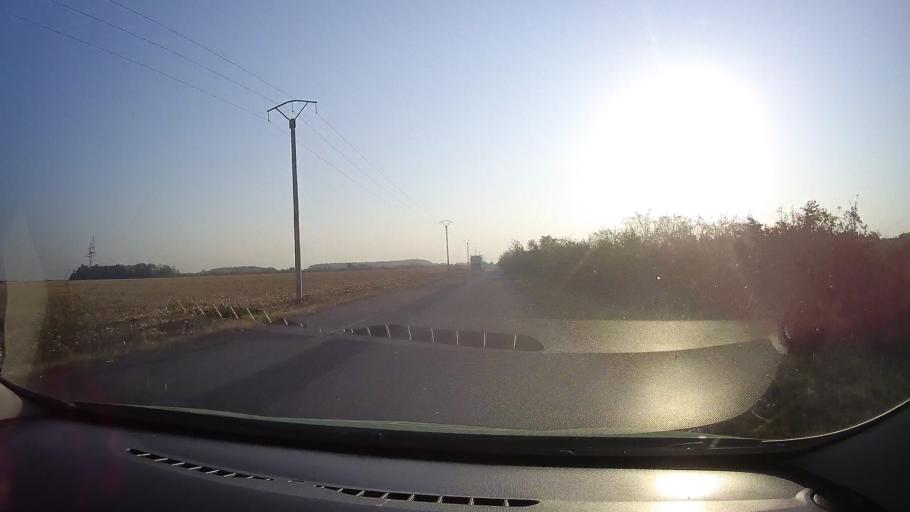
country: RO
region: Arad
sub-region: Comuna Zimandu Nou
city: Andrei Saguna
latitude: 46.3576
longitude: 21.3875
